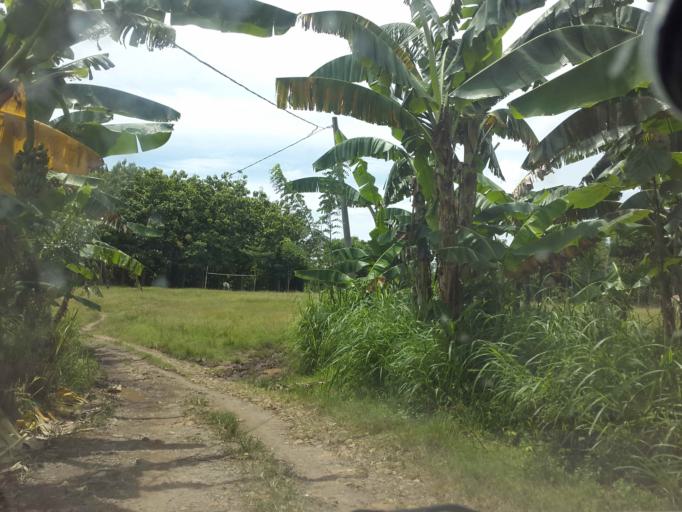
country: ID
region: Lampung
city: Sidorejo
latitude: -5.5786
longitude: 105.4497
